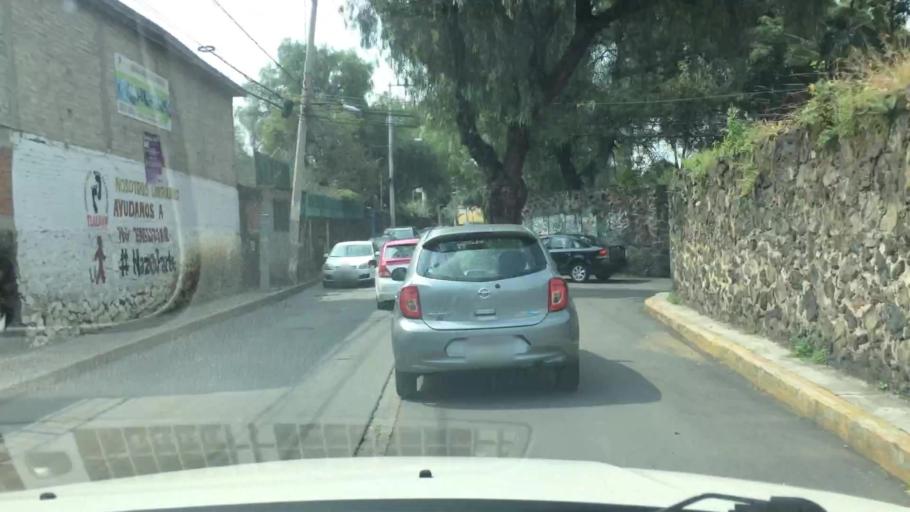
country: MX
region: Mexico City
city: Tlalpan
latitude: 19.2713
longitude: -99.1496
